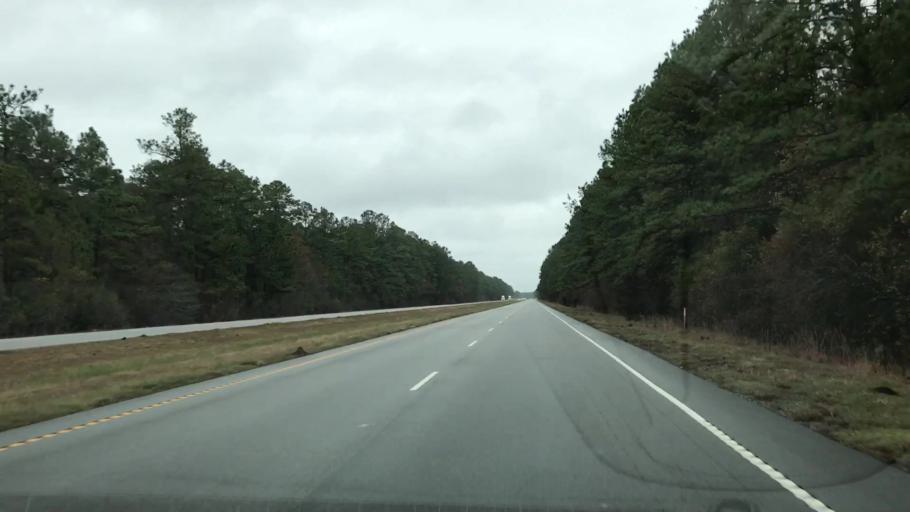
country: US
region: South Carolina
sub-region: Charleston County
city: Awendaw
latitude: 33.1579
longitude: -79.4279
